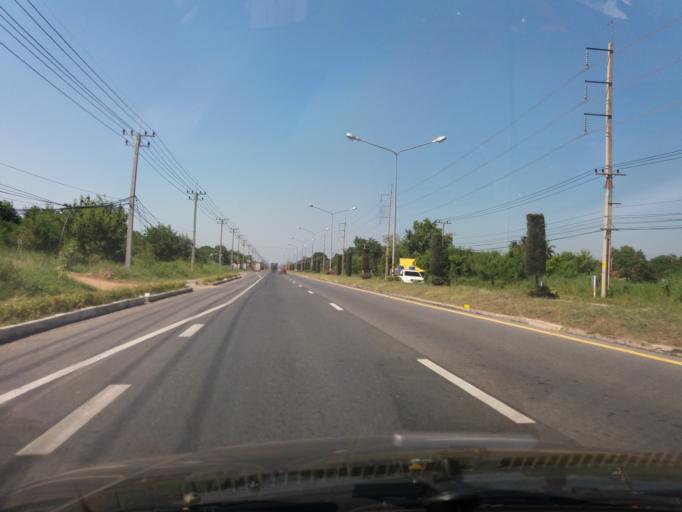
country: TH
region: Chai Nat
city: Chai Nat
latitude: 15.2192
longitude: 100.1142
